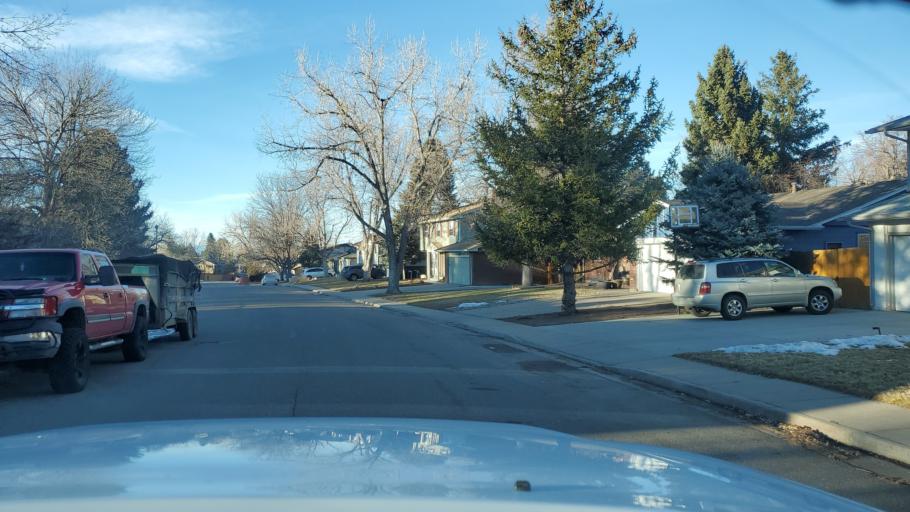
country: US
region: Colorado
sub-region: Arapahoe County
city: Castlewood
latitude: 39.5855
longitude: -104.9007
